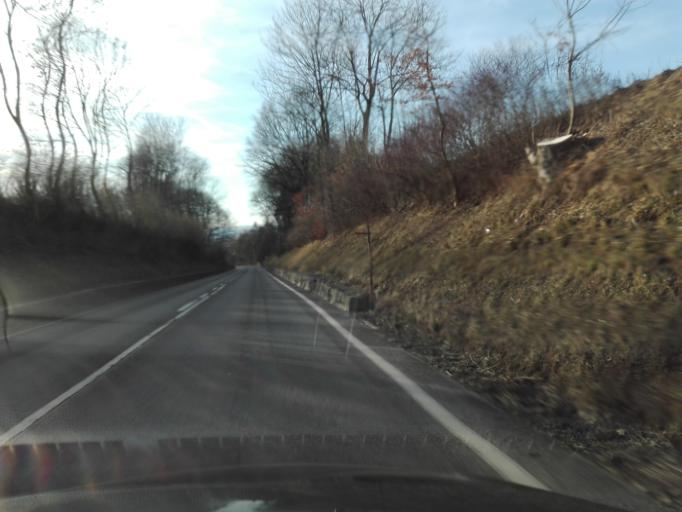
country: AT
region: Lower Austria
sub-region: Politischer Bezirk Amstetten
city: Sankt Valentin
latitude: 48.1881
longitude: 14.5554
